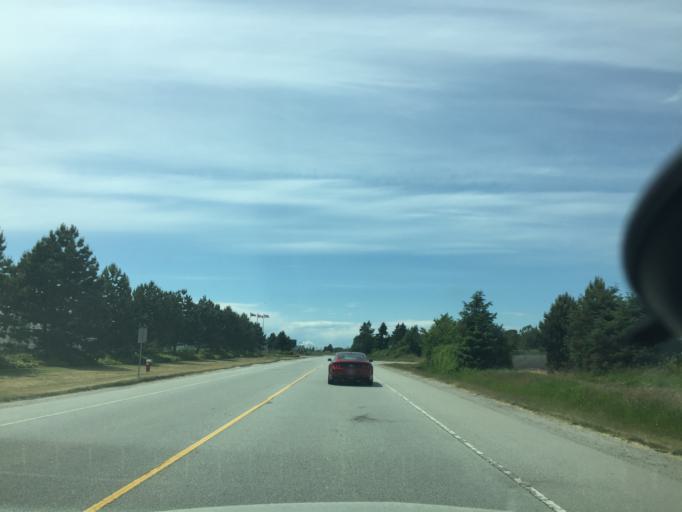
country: CA
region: British Columbia
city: Richmond
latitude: 49.2053
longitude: -123.1594
